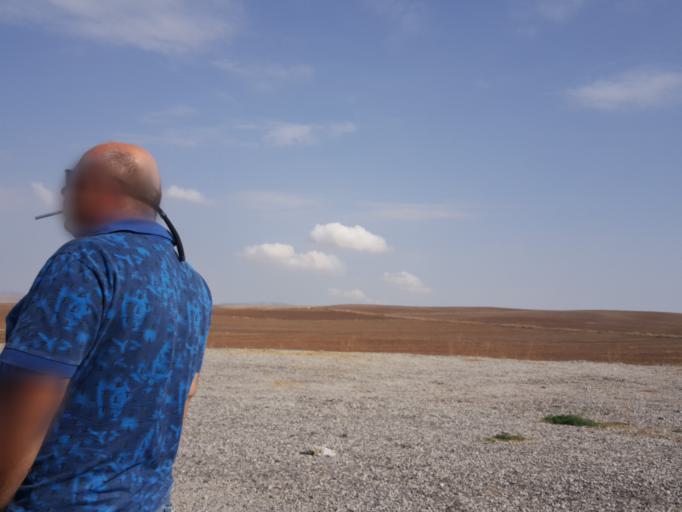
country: TR
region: Corum
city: Alaca
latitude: 40.1575
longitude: 34.8730
